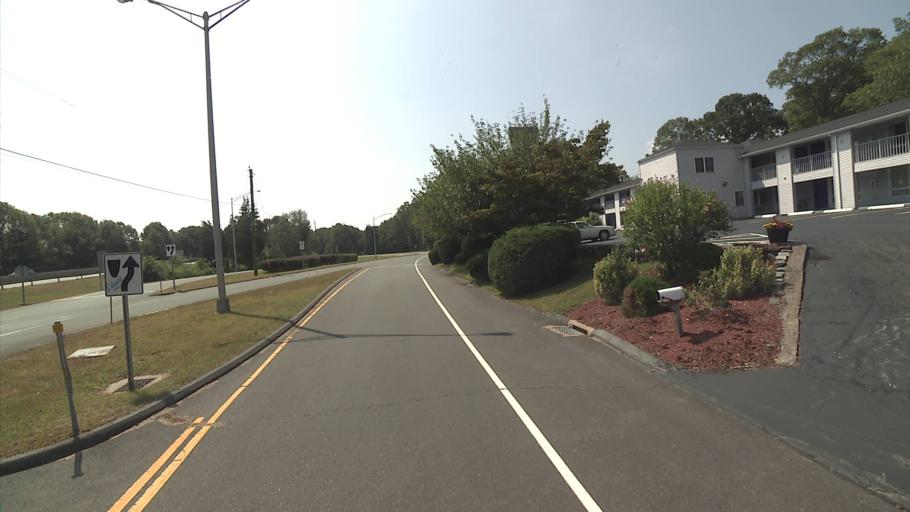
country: US
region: Connecticut
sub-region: Middlesex County
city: Old Saybrook Center
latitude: 41.3128
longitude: -72.3646
